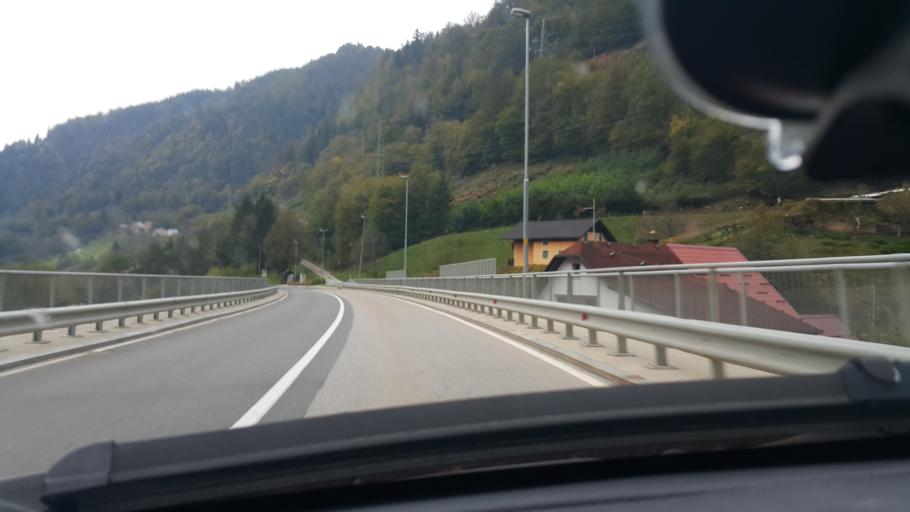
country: SI
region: Podvelka
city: Podvelka
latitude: 46.5931
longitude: 15.3412
